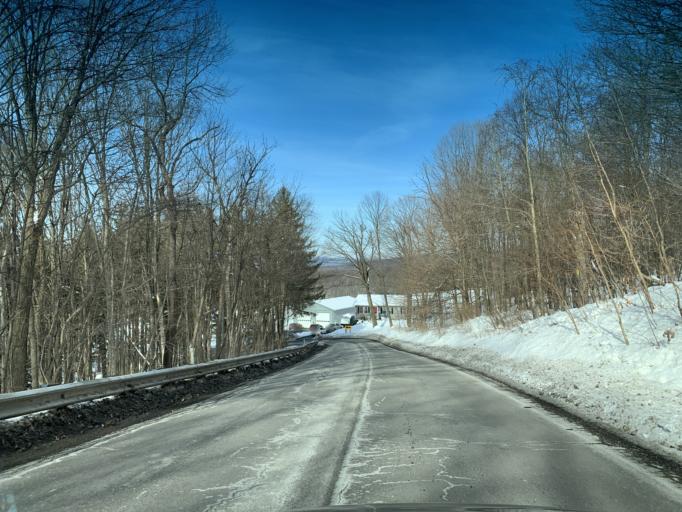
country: US
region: Maryland
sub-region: Allegany County
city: Frostburg
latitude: 39.6701
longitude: -78.8917
